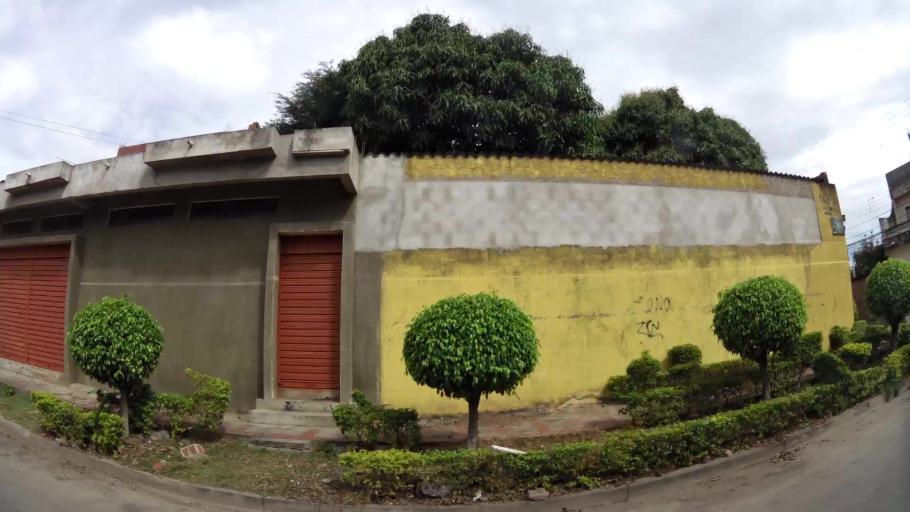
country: BO
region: Santa Cruz
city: Santa Cruz de la Sierra
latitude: -17.7785
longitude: -63.2084
